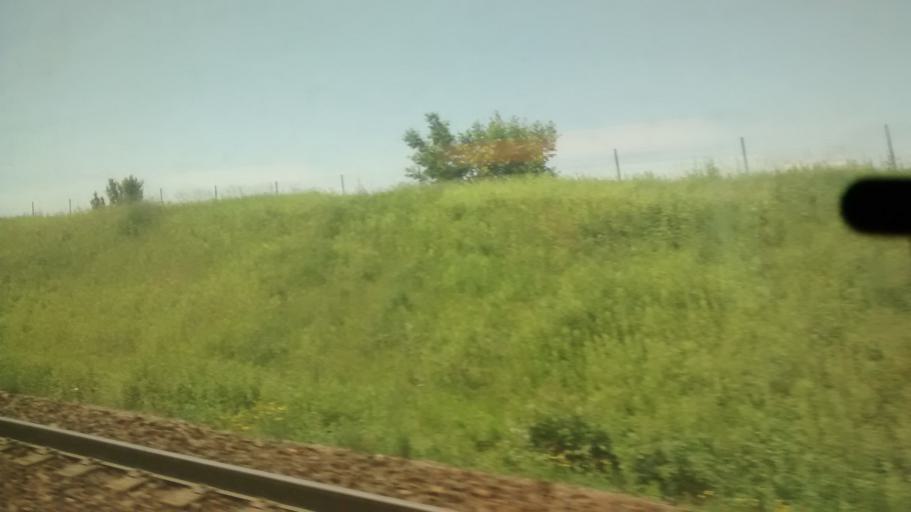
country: FR
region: Rhone-Alpes
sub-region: Departement du Rhone
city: Cailloux-sur-Fontaines
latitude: 45.8560
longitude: 4.8869
